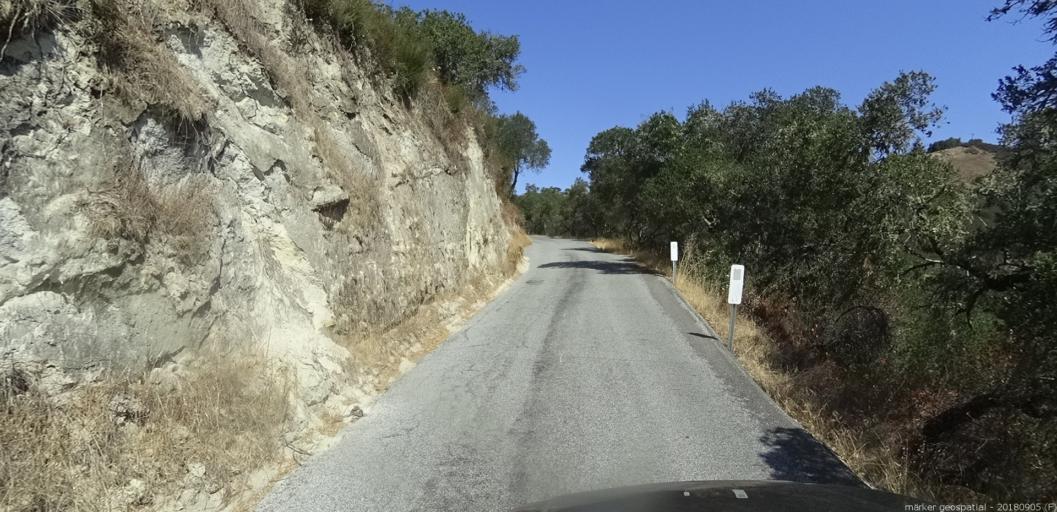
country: US
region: California
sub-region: Monterey County
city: Carmel Valley Village
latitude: 36.4218
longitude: -121.6796
